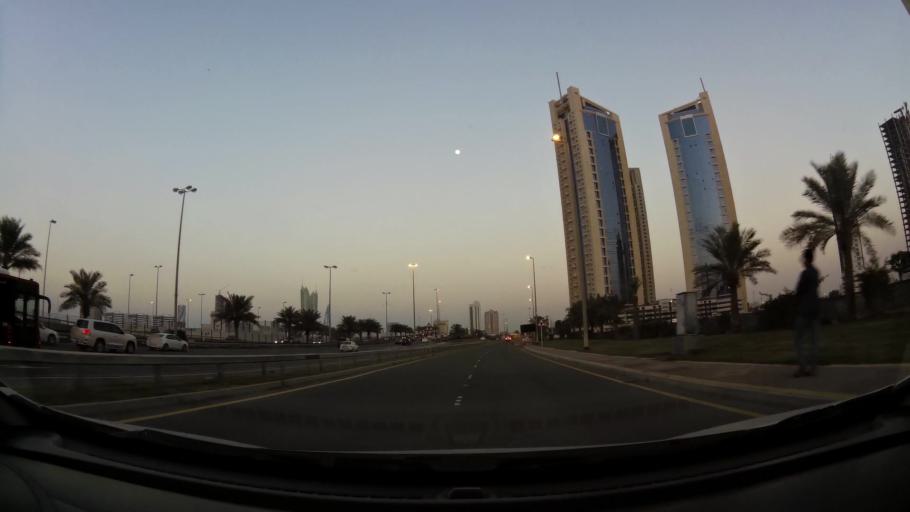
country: BH
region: Manama
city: Jidd Hafs
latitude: 26.2315
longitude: 50.5555
